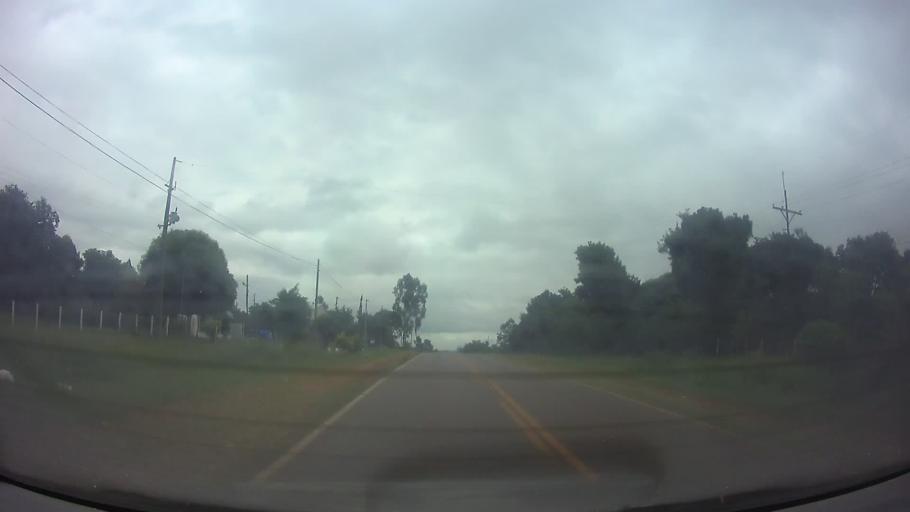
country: PY
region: Paraguari
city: Carapegua
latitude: -25.7816
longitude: -57.2236
